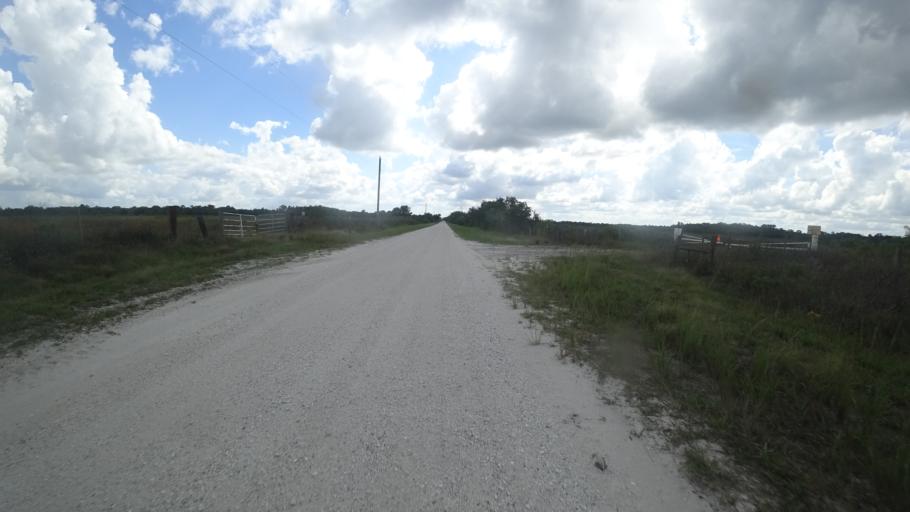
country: US
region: Florida
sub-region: Hillsborough County
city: Wimauma
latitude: 27.5626
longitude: -82.1742
